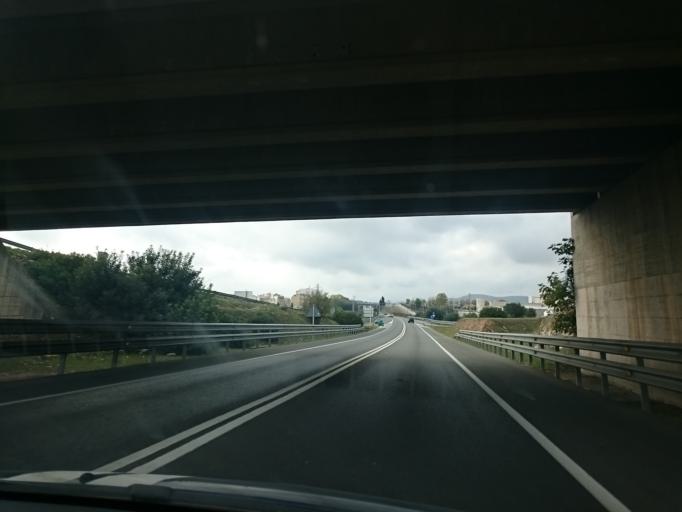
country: ES
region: Catalonia
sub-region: Provincia de Barcelona
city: Vilanova i la Geltru
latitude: 41.2367
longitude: 1.7341
